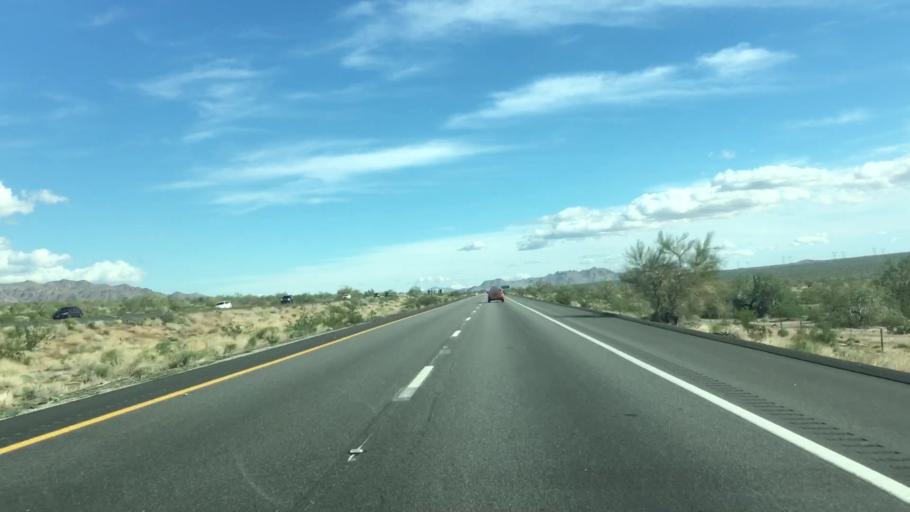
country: US
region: California
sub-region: Riverside County
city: Mecca
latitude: 33.6615
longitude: -115.8340
